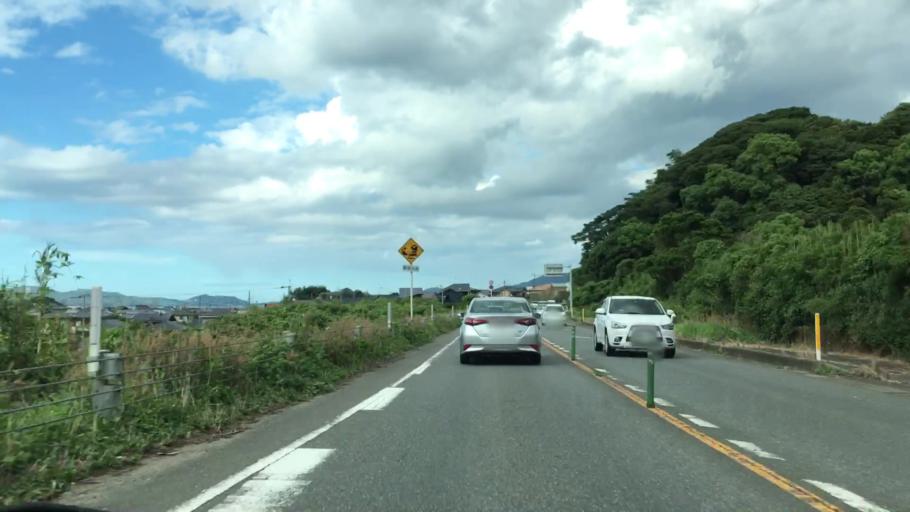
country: JP
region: Saga Prefecture
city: Karatsu
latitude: 33.4979
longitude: 130.0807
